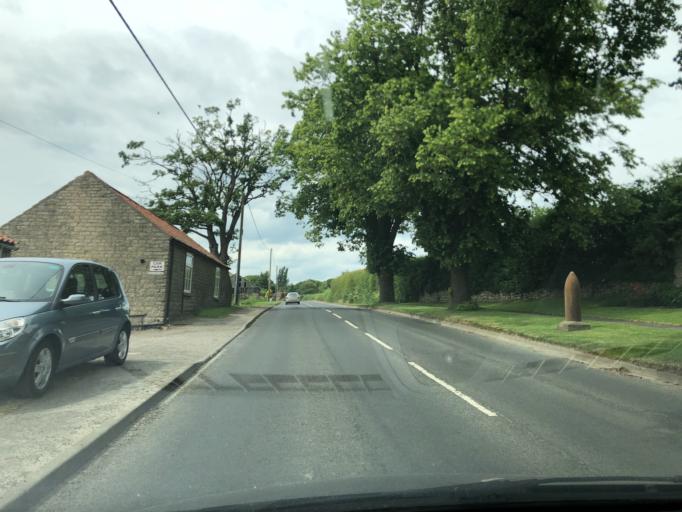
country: GB
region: England
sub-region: North Yorkshire
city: Pickering
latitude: 54.2589
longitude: -0.8037
